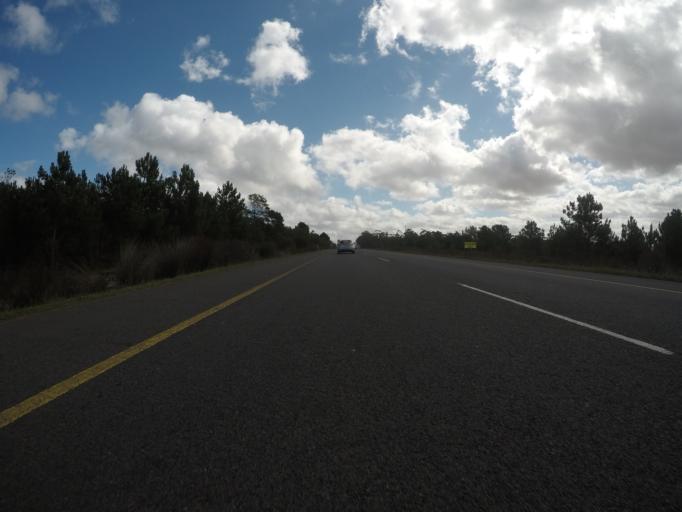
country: ZA
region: Western Cape
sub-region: Eden District Municipality
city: Riversdale
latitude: -34.2123
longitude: 21.5921
